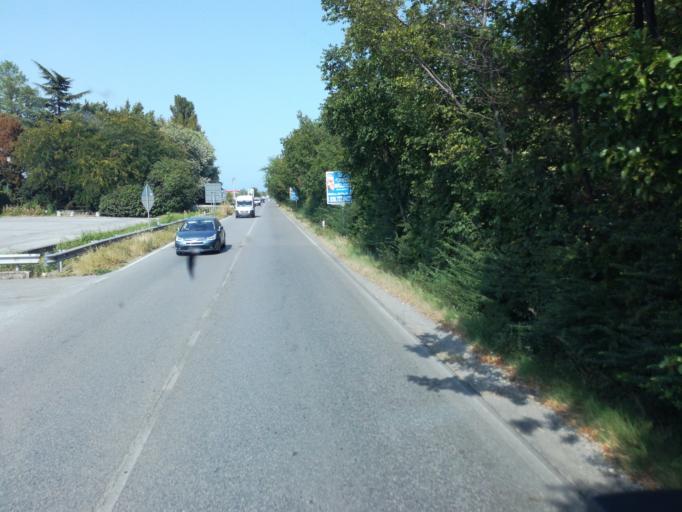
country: IT
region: Lombardy
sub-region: Provincia di Brescia
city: Dello
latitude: 45.4223
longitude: 10.0835
